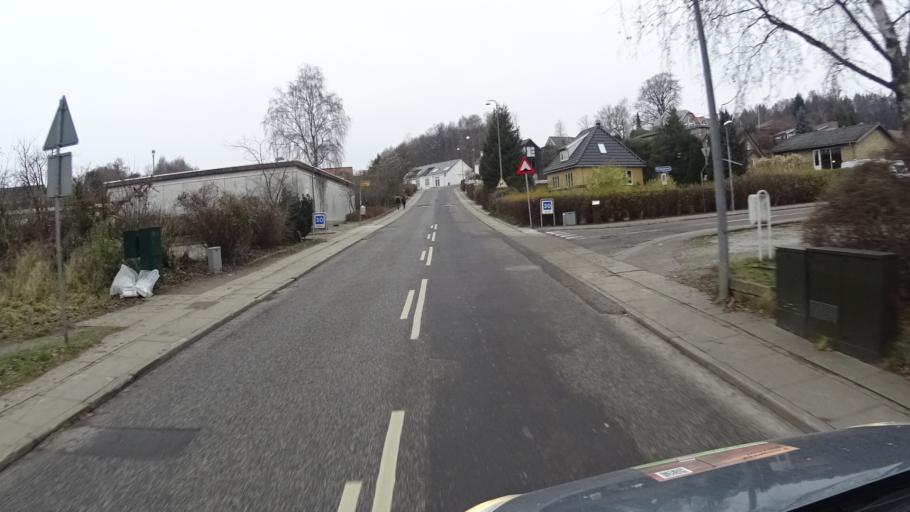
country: DK
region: South Denmark
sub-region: Vejle Kommune
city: Vejle
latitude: 55.7102
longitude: 9.6078
